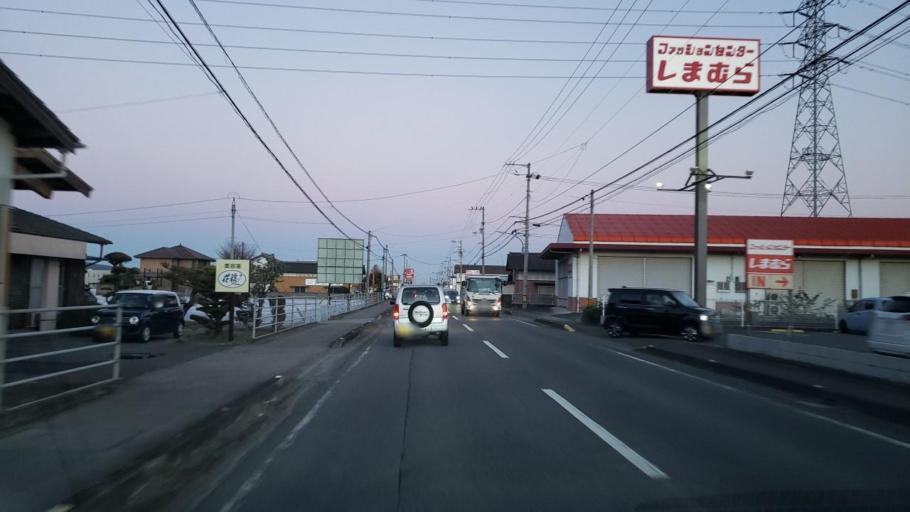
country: JP
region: Tokushima
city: Ishii
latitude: 34.1209
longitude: 134.4445
